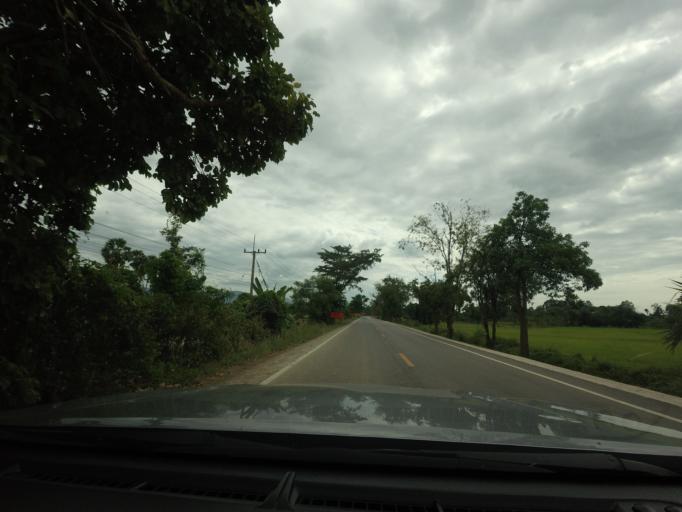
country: TH
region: Phitsanulok
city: Noen Maprang
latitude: 16.6940
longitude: 100.5953
